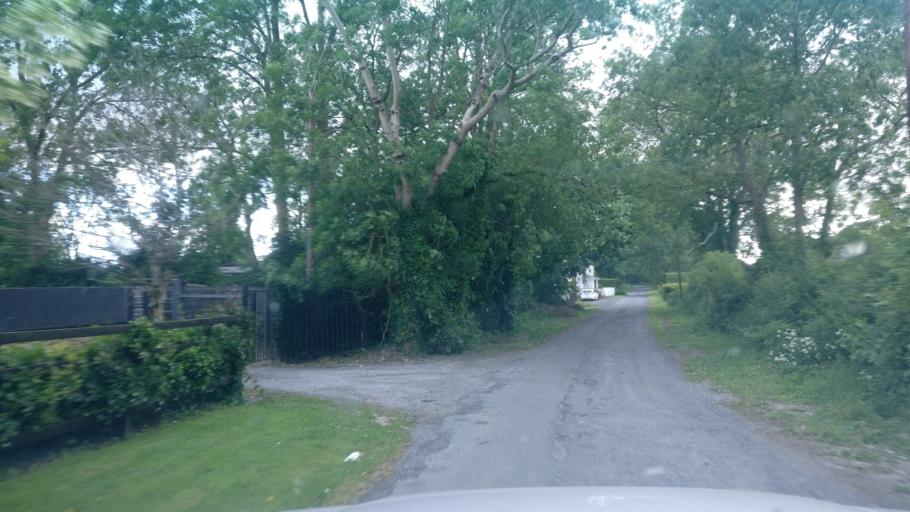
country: IE
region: Connaught
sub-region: County Galway
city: Ballinasloe
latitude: 53.2320
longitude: -8.2122
